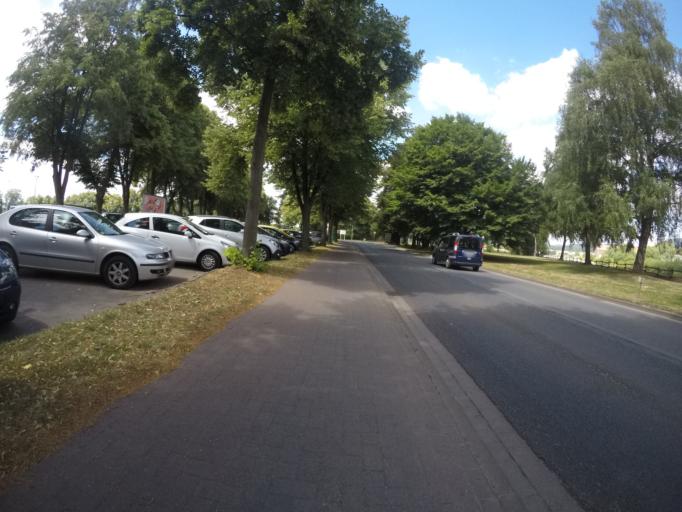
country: DE
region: Lower Saxony
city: Rinteln
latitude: 52.1902
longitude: 9.0757
